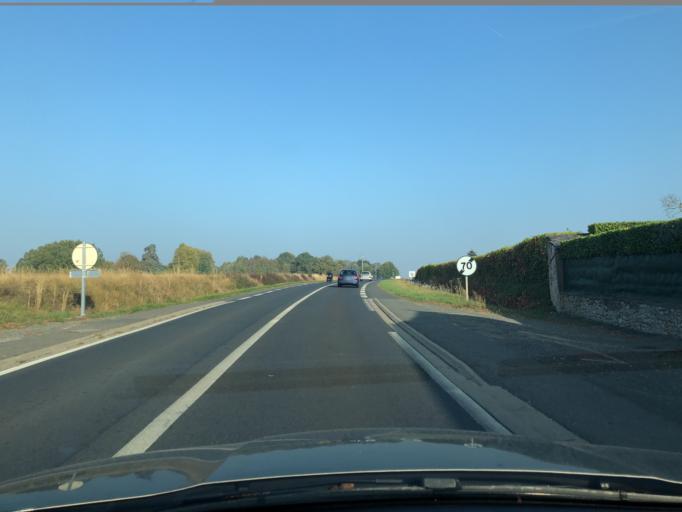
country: FR
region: Centre
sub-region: Departement d'Indre-et-Loire
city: Chanceaux-sur-Choisille
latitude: 47.4456
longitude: 0.6989
